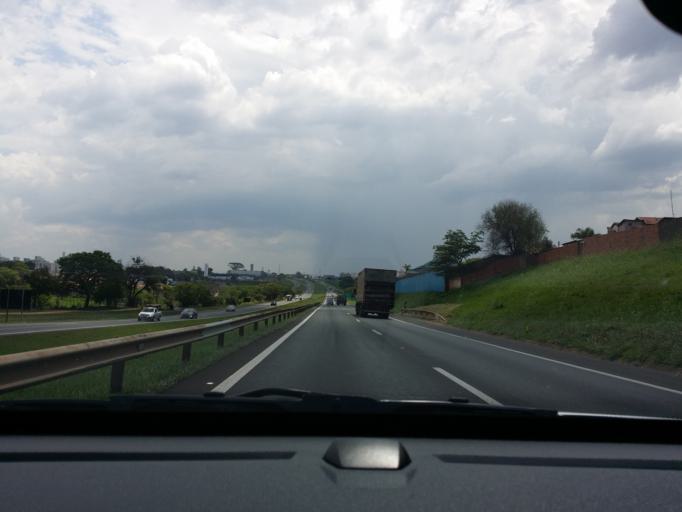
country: BR
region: Sao Paulo
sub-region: Rio Claro
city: Rio Claro
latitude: -22.4255
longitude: -47.5746
